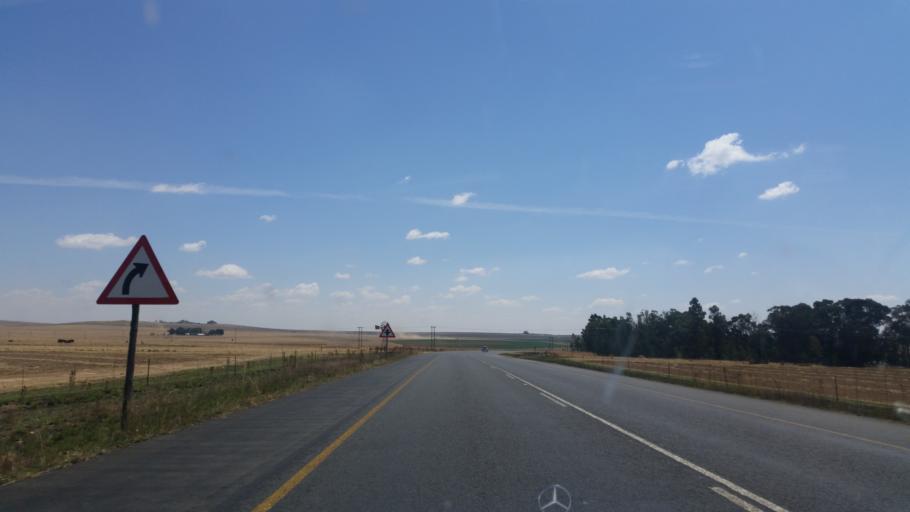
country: ZA
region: Orange Free State
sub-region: Thabo Mofutsanyana District Municipality
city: Bethlehem
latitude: -28.1072
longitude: 28.6645
